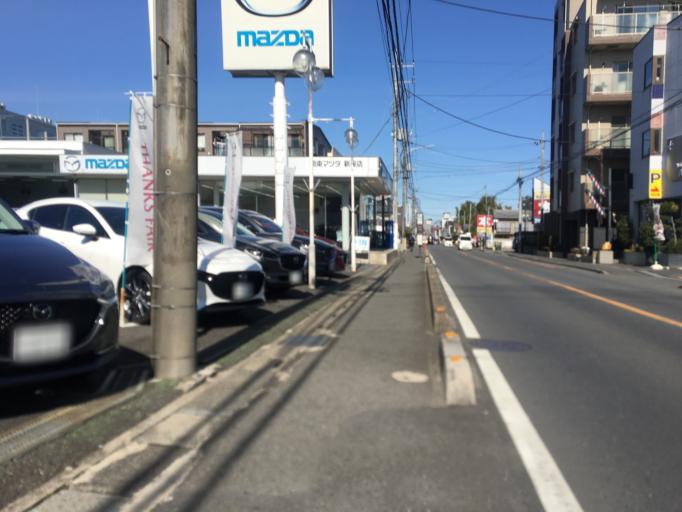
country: JP
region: Saitama
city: Shiki
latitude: 35.8113
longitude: 139.5662
